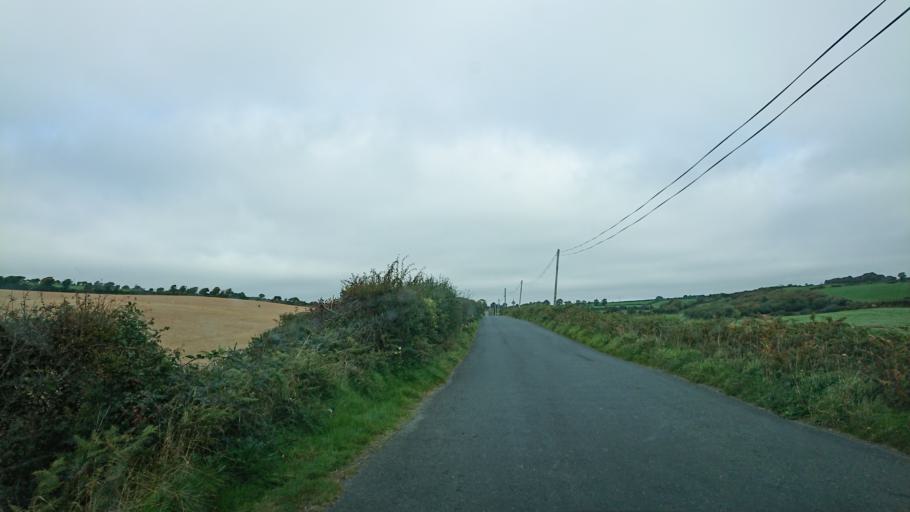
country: IE
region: Munster
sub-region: Waterford
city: Tra Mhor
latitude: 52.1826
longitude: -7.1146
